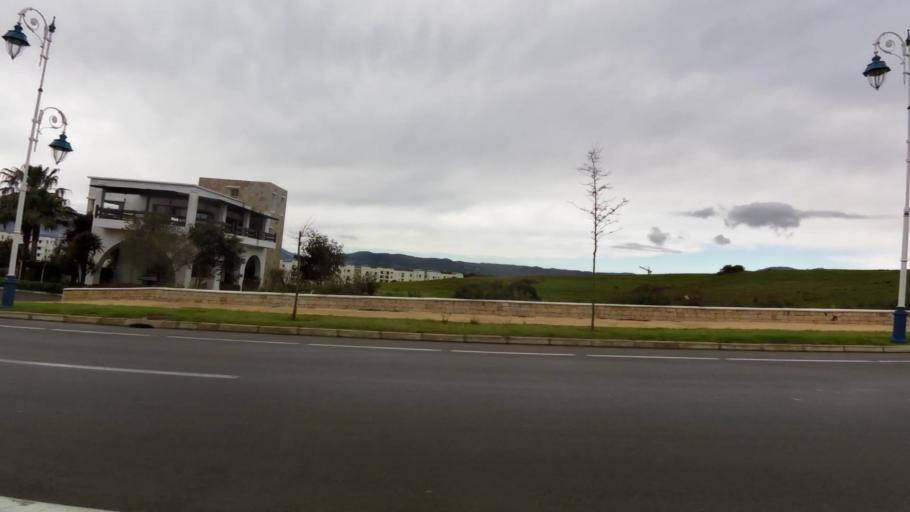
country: MA
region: Tanger-Tetouan
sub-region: Tetouan
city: Martil
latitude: 35.6654
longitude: -5.3031
